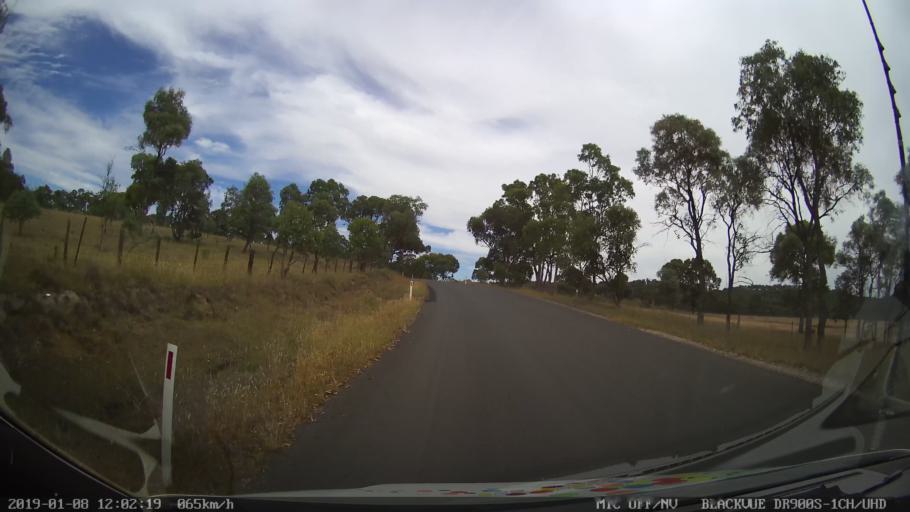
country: AU
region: New South Wales
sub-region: Armidale Dumaresq
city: Armidale
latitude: -30.4550
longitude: 151.6048
